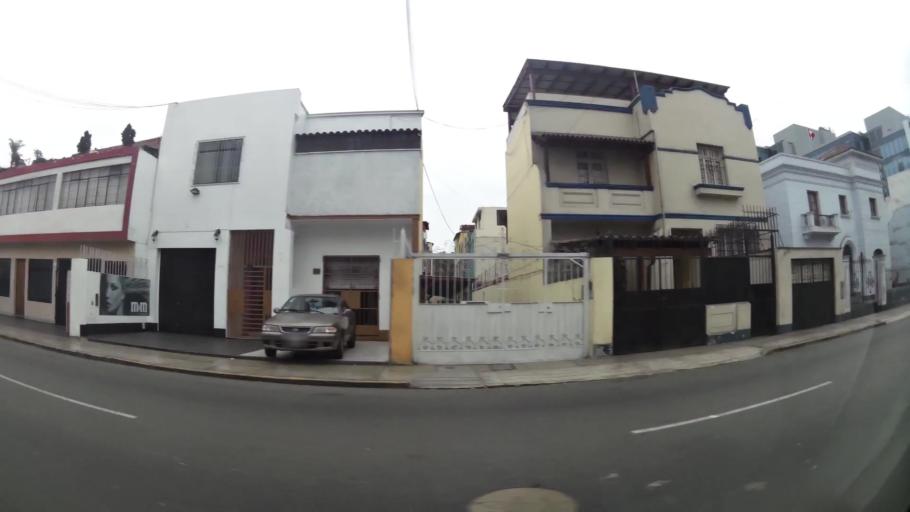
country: PE
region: Lima
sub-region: Lima
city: San Isidro
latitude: -12.0983
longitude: -77.0329
